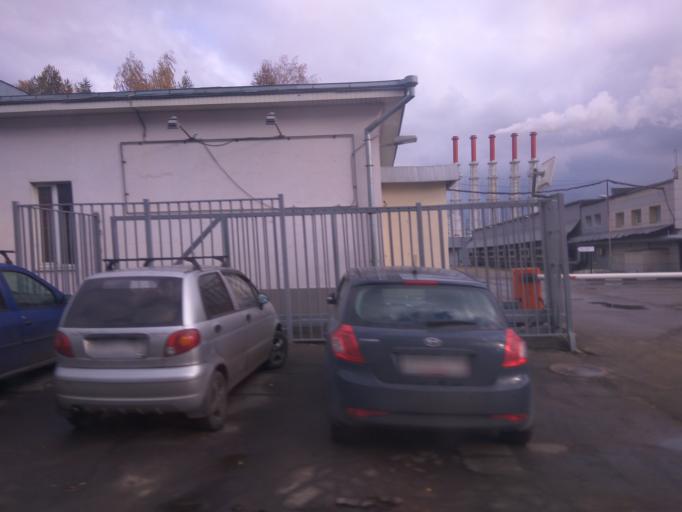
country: RU
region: Moscow
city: Tsaritsyno
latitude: 55.6299
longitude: 37.6394
